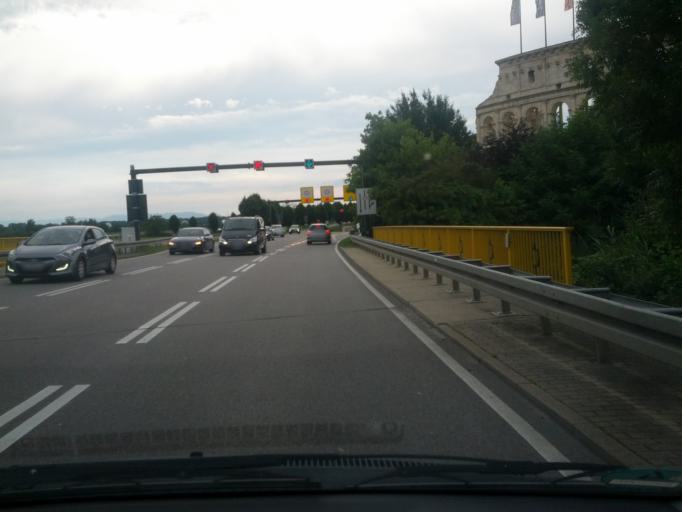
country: DE
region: Baden-Wuerttemberg
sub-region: Freiburg Region
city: Rust
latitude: 48.2588
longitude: 7.7254
